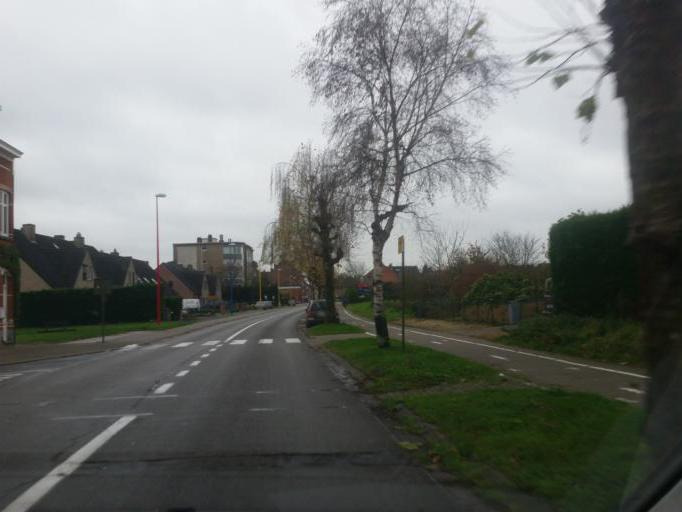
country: BE
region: Flanders
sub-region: Provincie Vlaams-Brabant
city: Grimbergen
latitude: 50.9151
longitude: 4.3592
